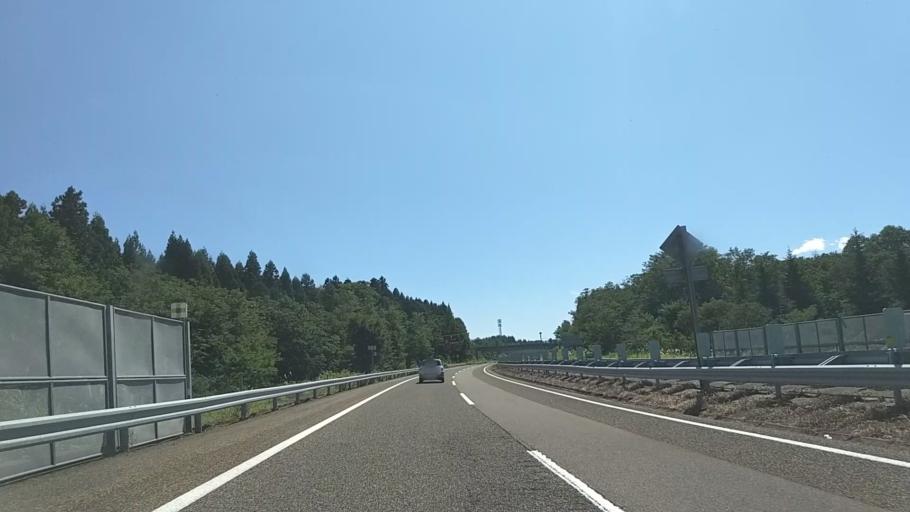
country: JP
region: Niigata
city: Arai
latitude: 36.9756
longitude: 138.2216
